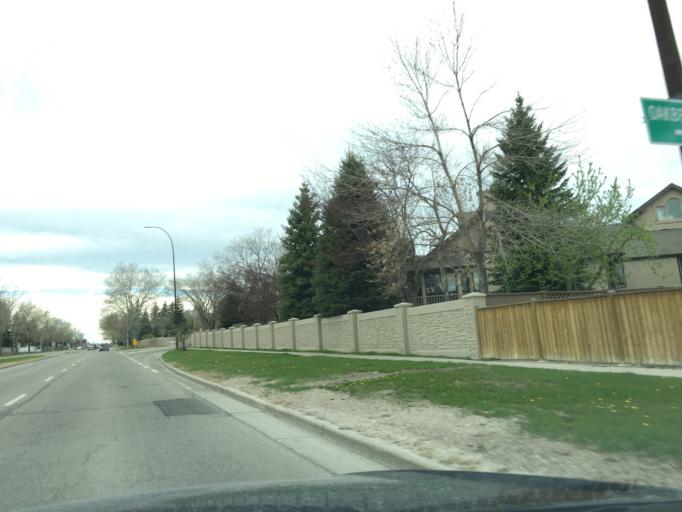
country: CA
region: Alberta
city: Calgary
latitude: 50.9614
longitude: -114.1104
